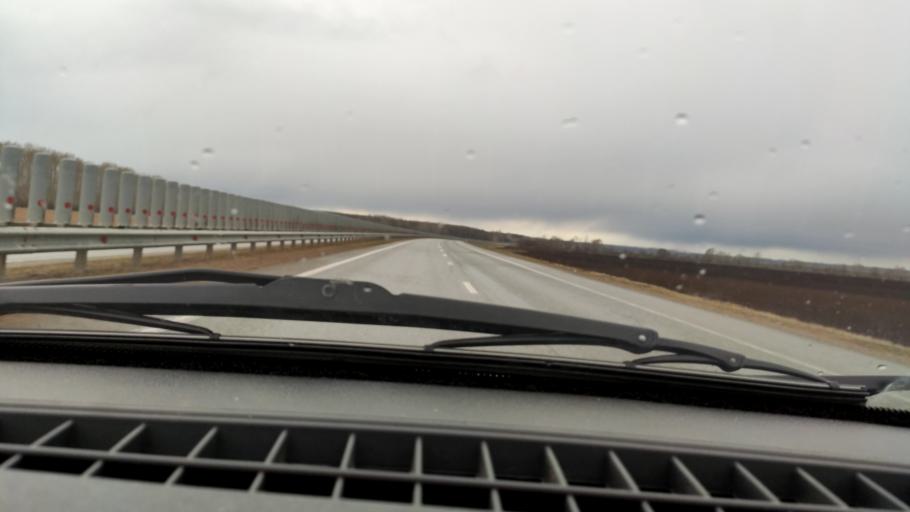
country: RU
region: Bashkortostan
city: Kushnarenkovo
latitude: 55.0610
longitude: 55.3886
